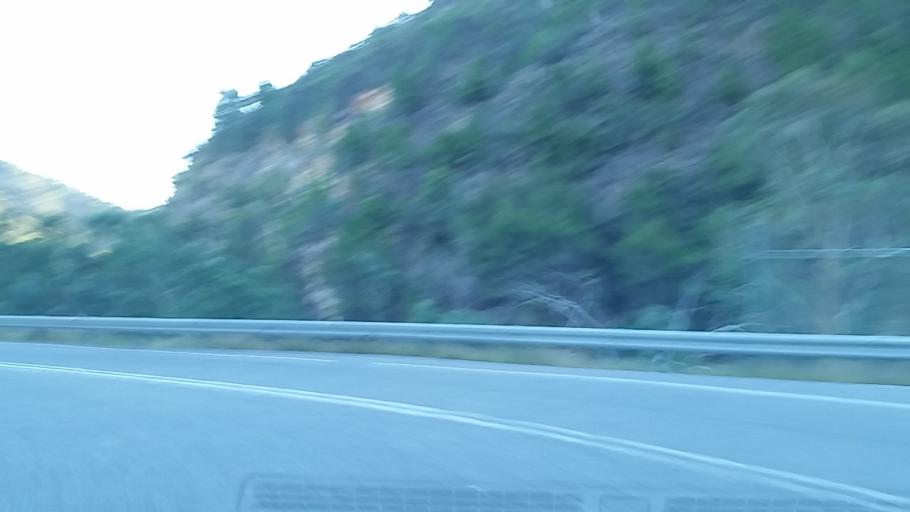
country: AU
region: South Australia
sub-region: Campbelltown
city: Athelstone
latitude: -34.8565
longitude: 138.7311
